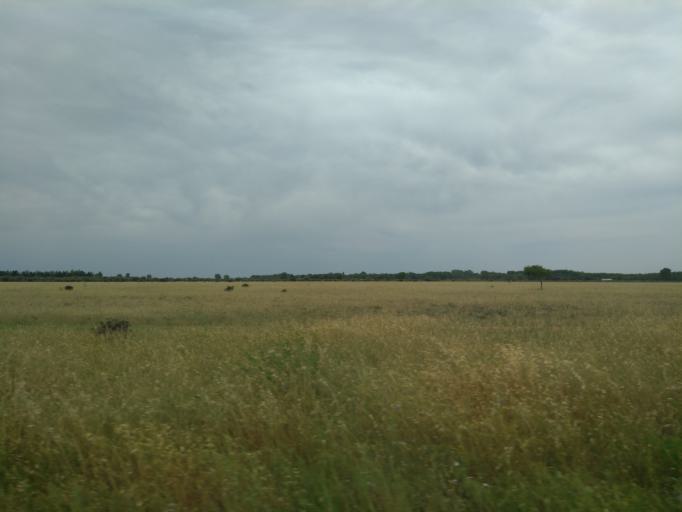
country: FR
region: Provence-Alpes-Cote d'Azur
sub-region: Departement des Bouches-du-Rhone
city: Miramas
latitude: 43.6244
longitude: 5.0165
